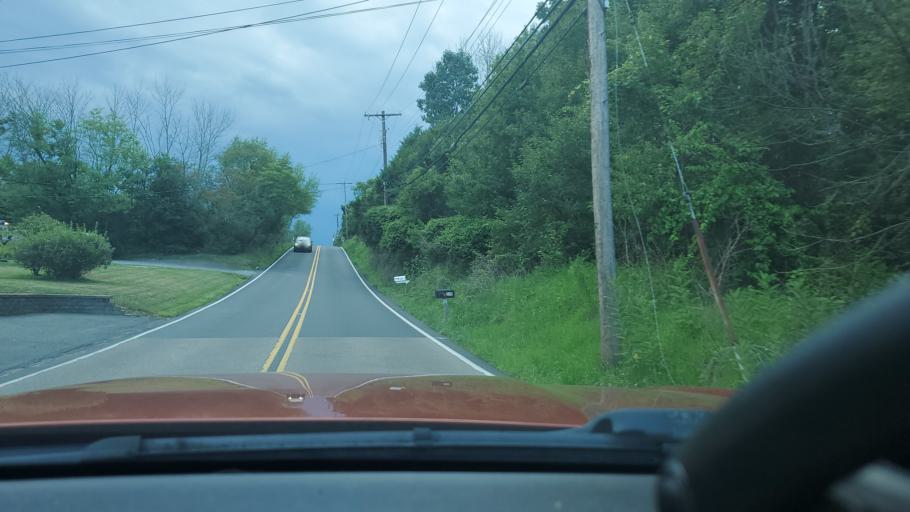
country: US
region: Pennsylvania
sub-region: Montgomery County
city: Limerick
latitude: 40.2515
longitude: -75.5212
